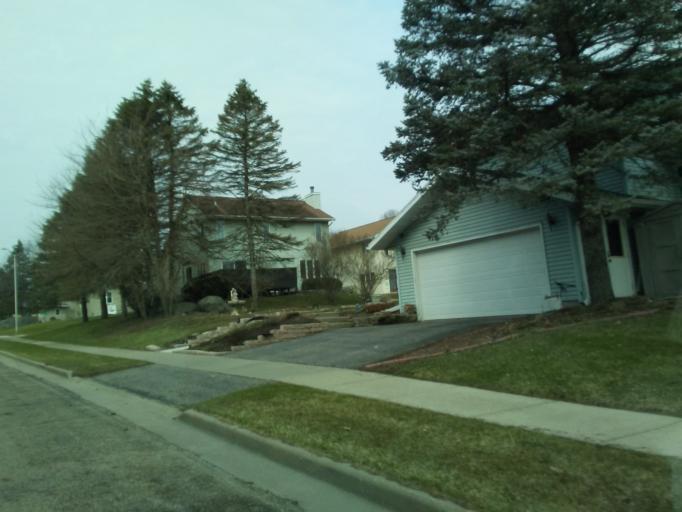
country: US
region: Wisconsin
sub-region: Columbia County
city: Lodi
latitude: 43.3125
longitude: -89.5373
